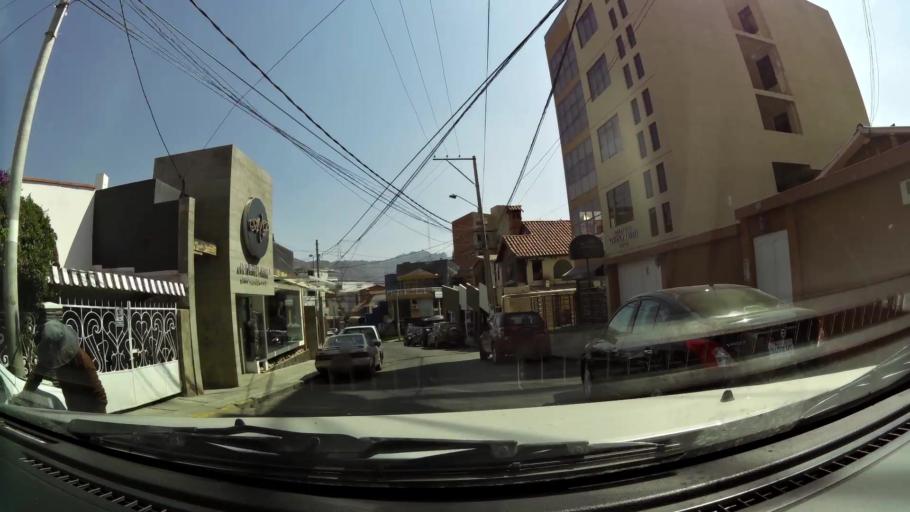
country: BO
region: La Paz
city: La Paz
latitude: -16.5411
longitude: -68.0793
